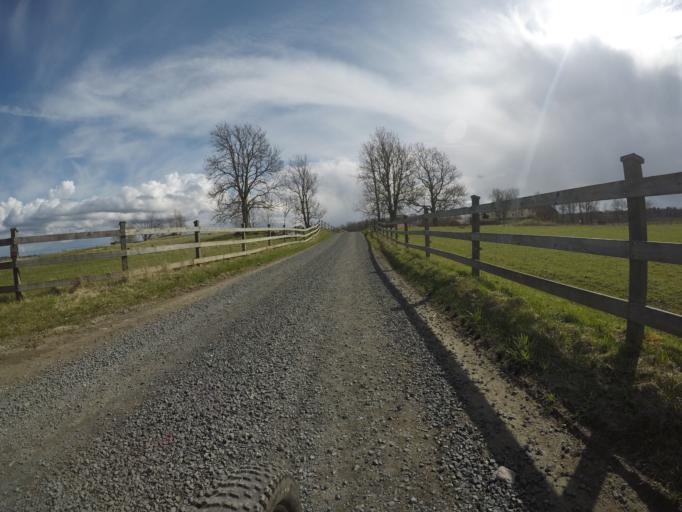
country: SE
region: Vaestmanland
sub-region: Kungsors Kommun
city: Kungsoer
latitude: 59.2828
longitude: 16.1532
